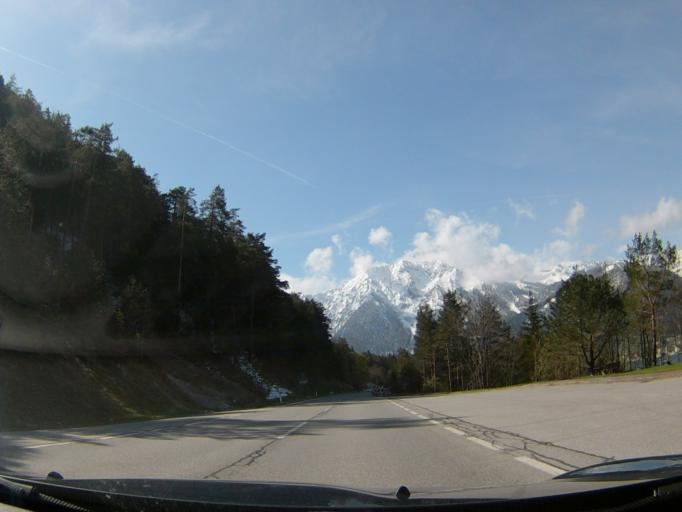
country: AT
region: Tyrol
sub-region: Politischer Bezirk Schwaz
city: Achenkirch
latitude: 47.4551
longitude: 11.7149
